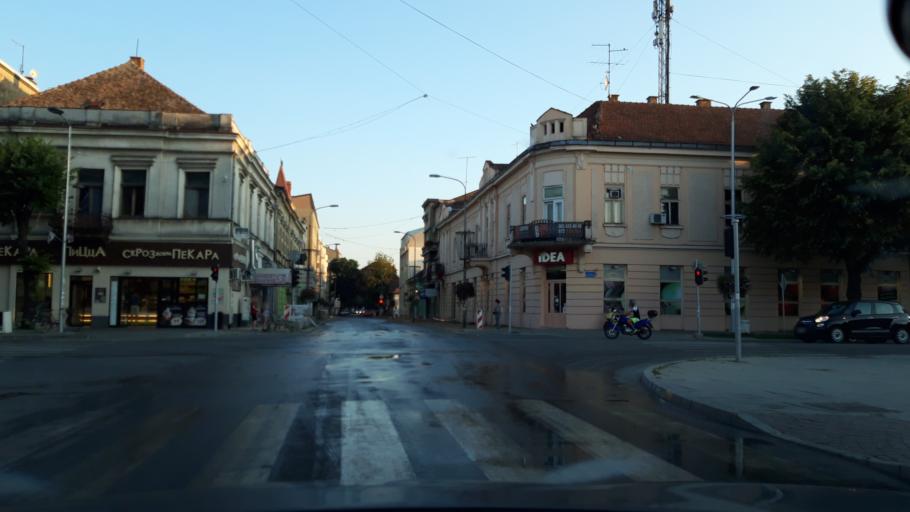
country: RS
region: Autonomna Pokrajina Vojvodina
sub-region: Sremski Okrug
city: Ruma
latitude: 45.0081
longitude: 19.8227
